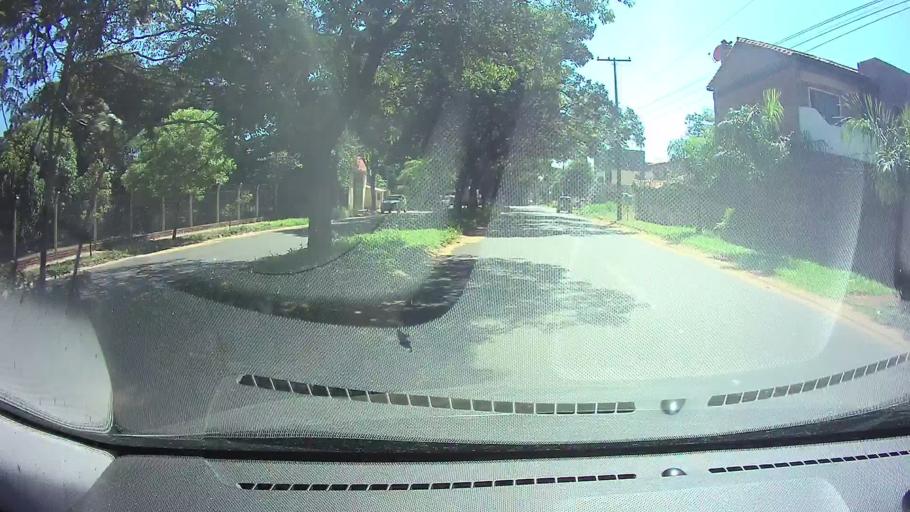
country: PY
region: Central
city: Fernando de la Mora
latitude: -25.2912
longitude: -57.5217
